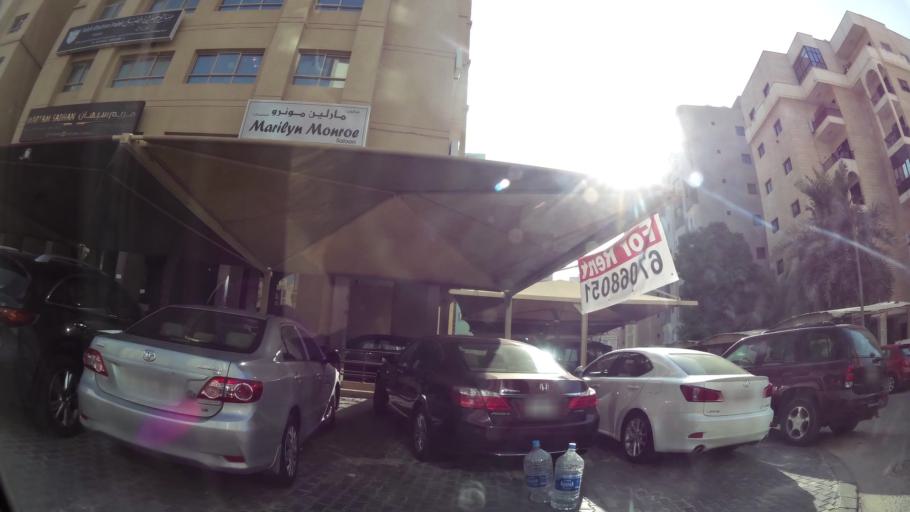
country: KW
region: Muhafazat Hawalli
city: As Salimiyah
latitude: 29.3398
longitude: 48.0919
